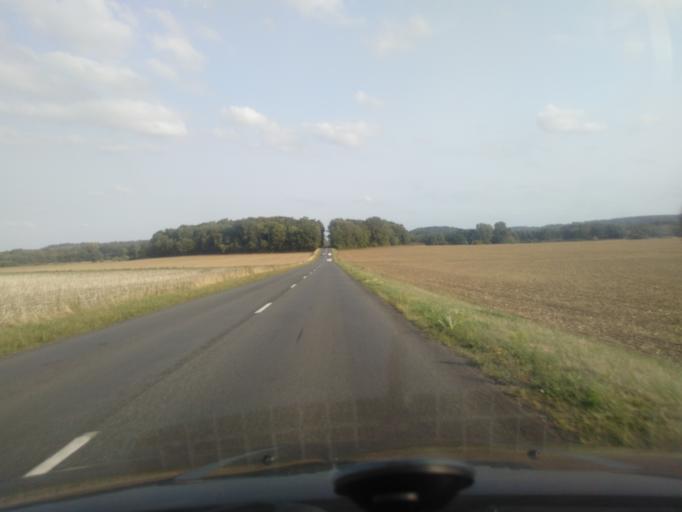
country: FR
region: Picardie
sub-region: Departement de l'Aisne
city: Bruyeres-et-Montberault
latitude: 49.5418
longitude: 3.6378
